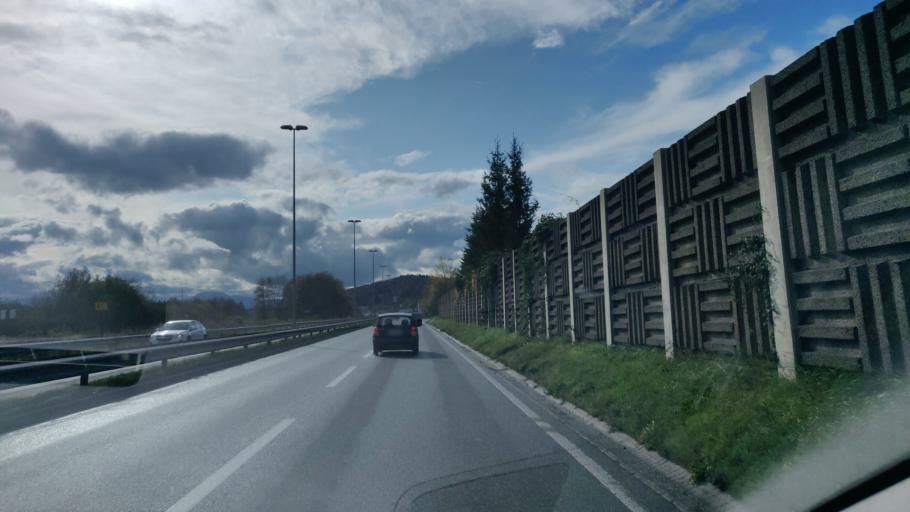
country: SI
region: Trzin
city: Trzin
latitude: 46.1261
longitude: 14.5573
